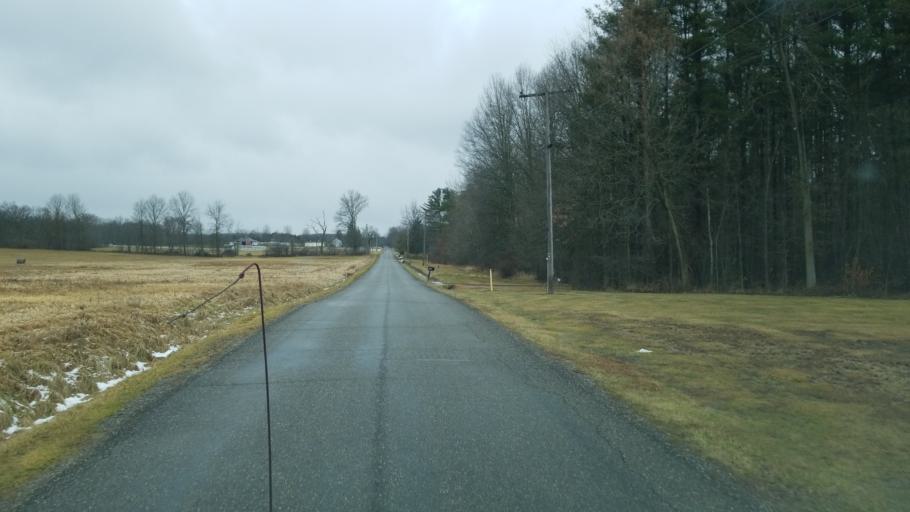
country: US
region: Ohio
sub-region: Trumbull County
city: Leavittsburg
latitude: 41.3393
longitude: -80.9678
